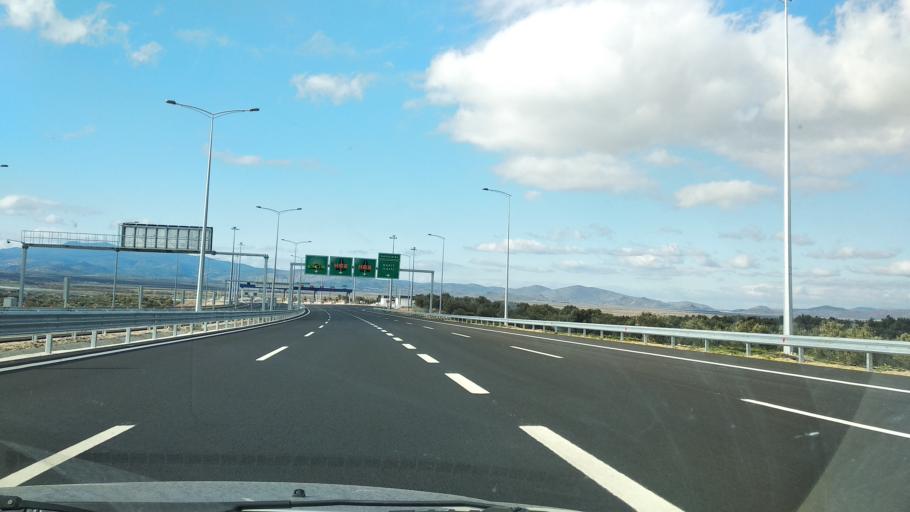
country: TR
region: Izmir
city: Zeytindag
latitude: 38.9726
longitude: 27.0579
